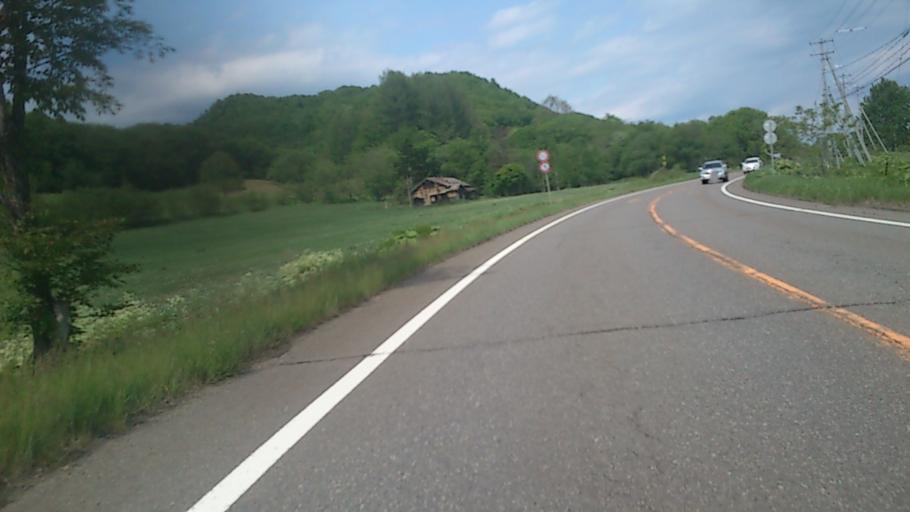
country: JP
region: Hokkaido
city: Kitami
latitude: 43.3424
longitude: 143.7631
